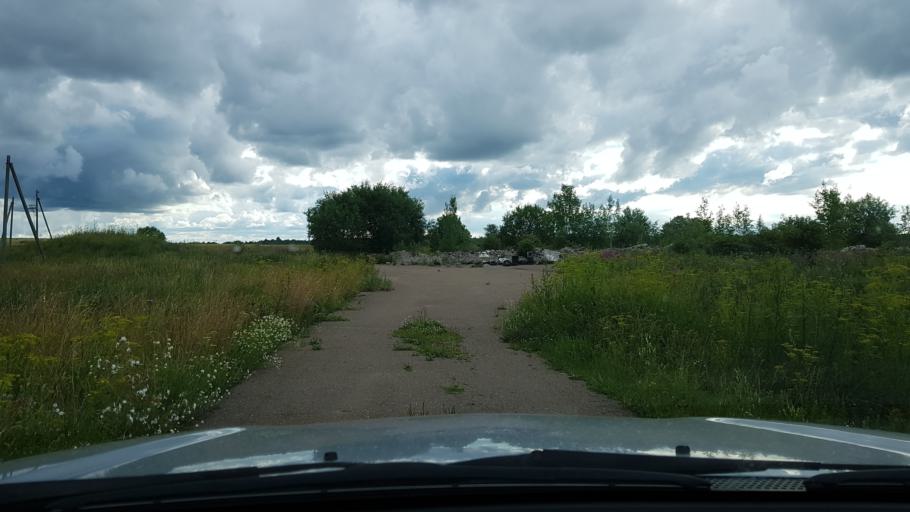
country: EE
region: Ida-Virumaa
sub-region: Narva-Joesuu linn
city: Narva-Joesuu
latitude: 59.3892
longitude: 27.9896
